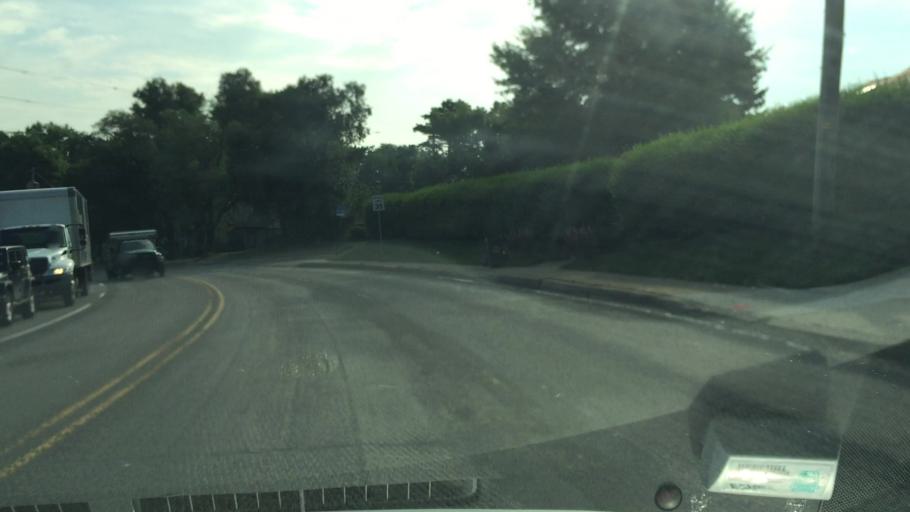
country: US
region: Pennsylvania
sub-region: Allegheny County
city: Heidelberg
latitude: 40.3723
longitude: -80.0770
